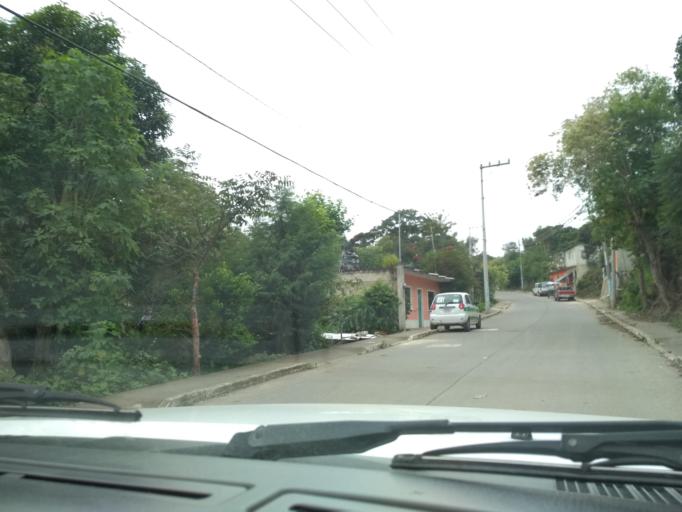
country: MX
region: Veracruz
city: El Castillo
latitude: 19.5769
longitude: -96.8652
